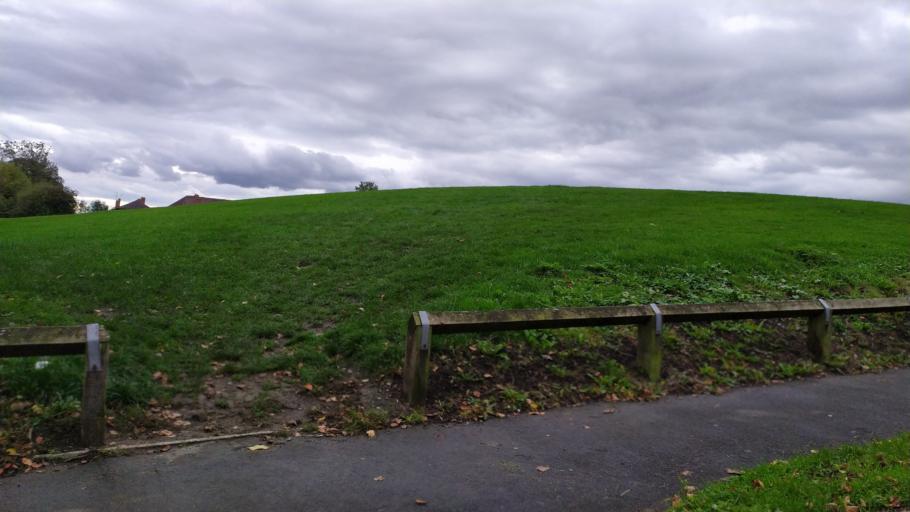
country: GB
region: England
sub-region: City and Borough of Leeds
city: Chapel Allerton
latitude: 53.8249
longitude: -1.5411
